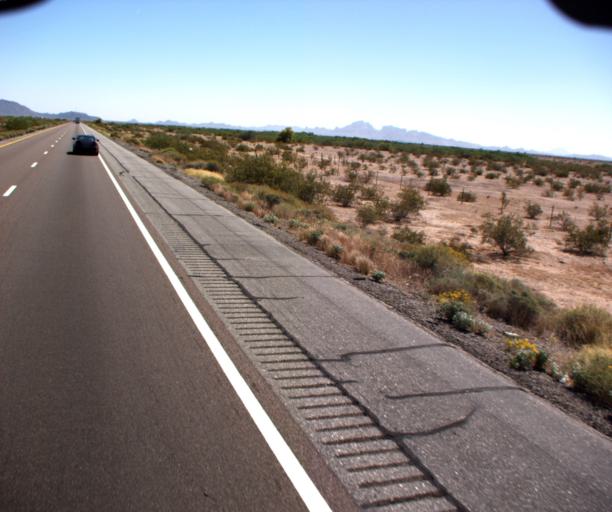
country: US
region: Arizona
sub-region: La Paz County
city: Salome
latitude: 33.5482
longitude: -113.2183
